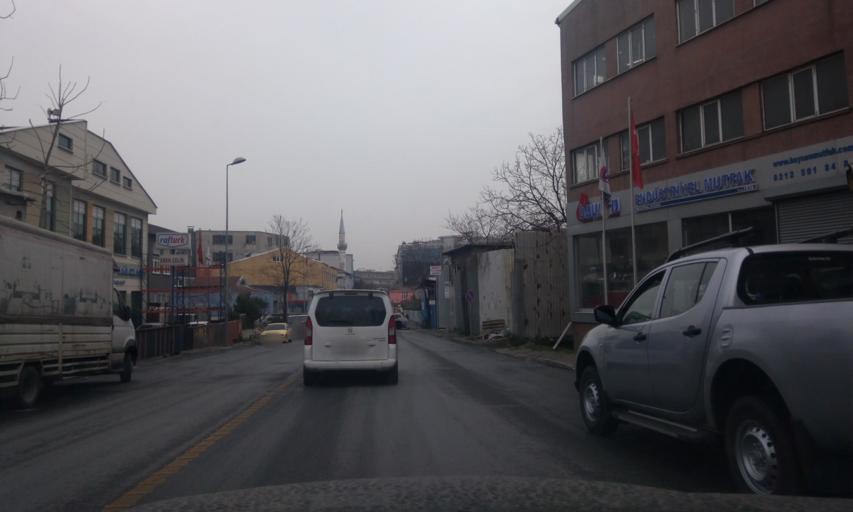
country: TR
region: Istanbul
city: Esenler
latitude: 41.0434
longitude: 28.9141
